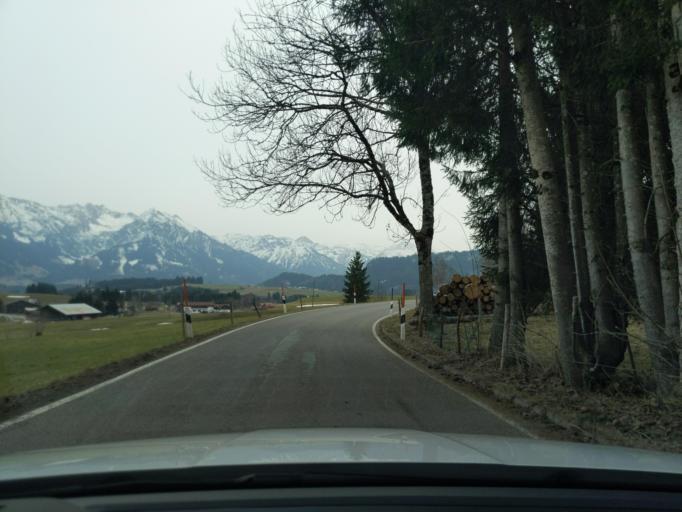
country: DE
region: Bavaria
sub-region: Swabia
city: Bolsterlang
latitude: 47.4654
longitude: 10.2309
